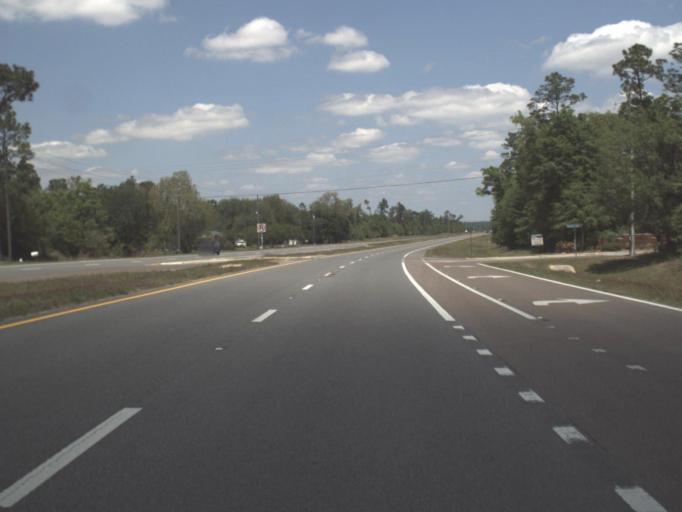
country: US
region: Florida
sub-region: Santa Rosa County
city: Point Baker
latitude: 30.6928
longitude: -87.0533
